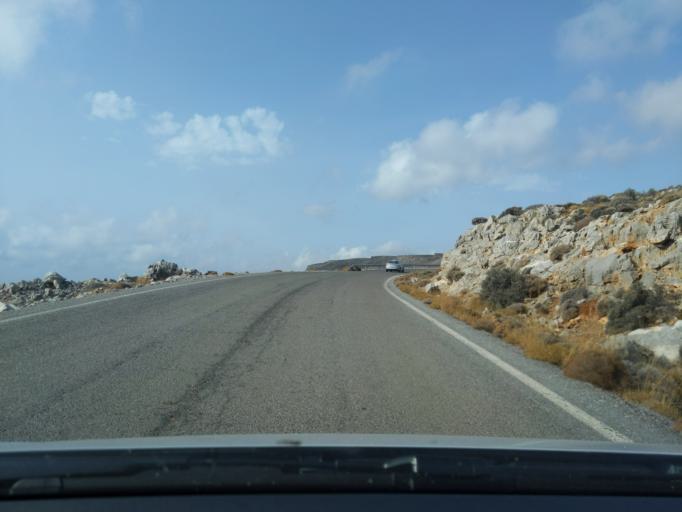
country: GR
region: Crete
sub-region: Nomos Lasithiou
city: Palekastro
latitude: 35.0848
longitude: 26.2628
